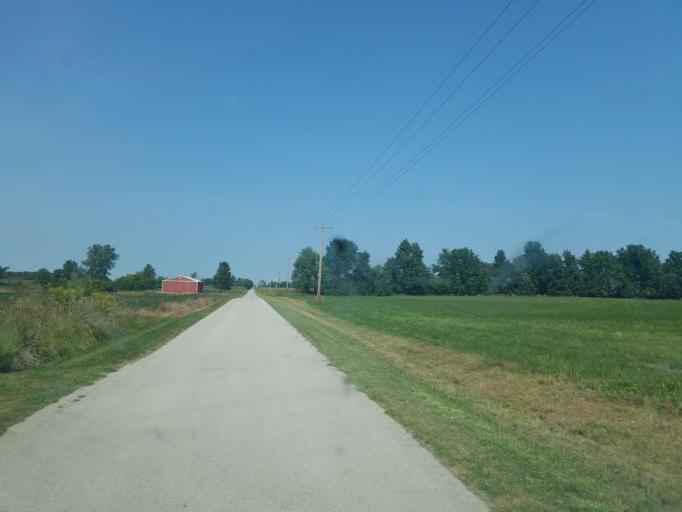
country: US
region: Ohio
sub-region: Crawford County
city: Bucyrus
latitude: 40.8829
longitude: -83.1126
